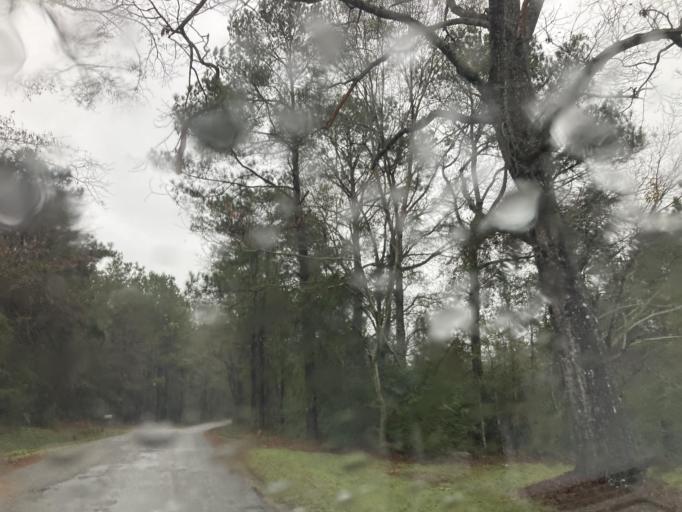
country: US
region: Mississippi
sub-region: Forrest County
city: Rawls Springs
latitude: 31.4831
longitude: -89.3846
